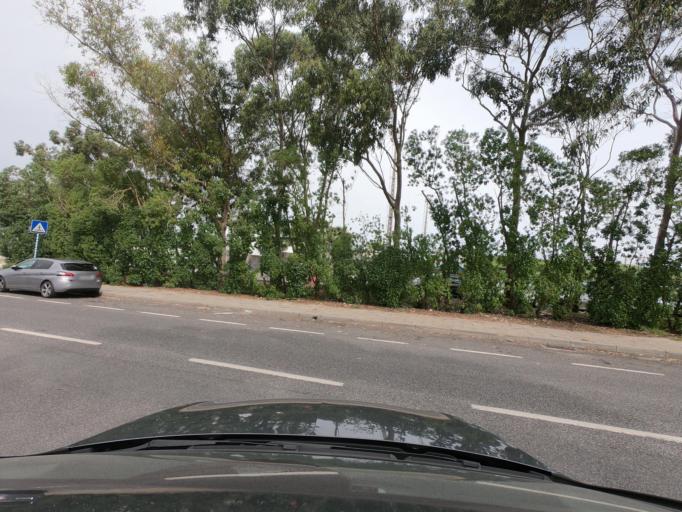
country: PT
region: Lisbon
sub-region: Oeiras
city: Porto Salvo
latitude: 38.7206
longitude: -9.2930
